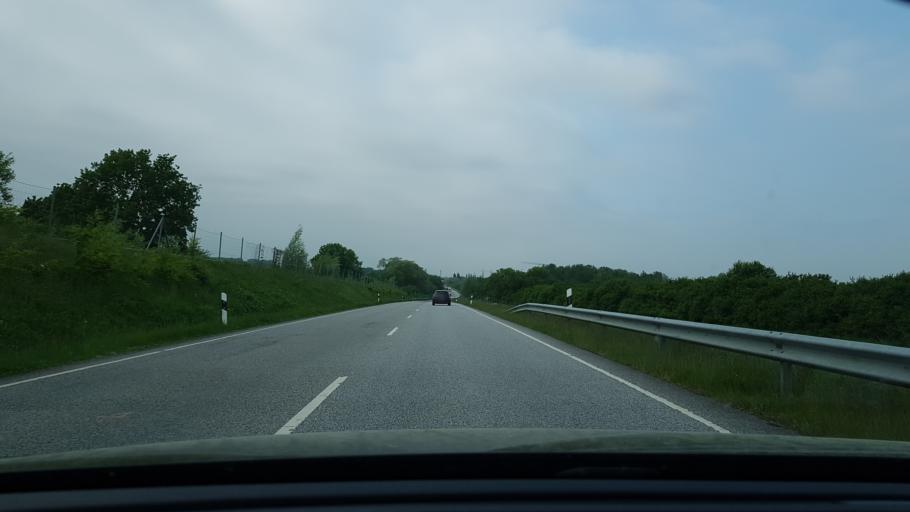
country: DE
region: Schleswig-Holstein
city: Luebeck
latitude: 53.8189
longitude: 10.6932
